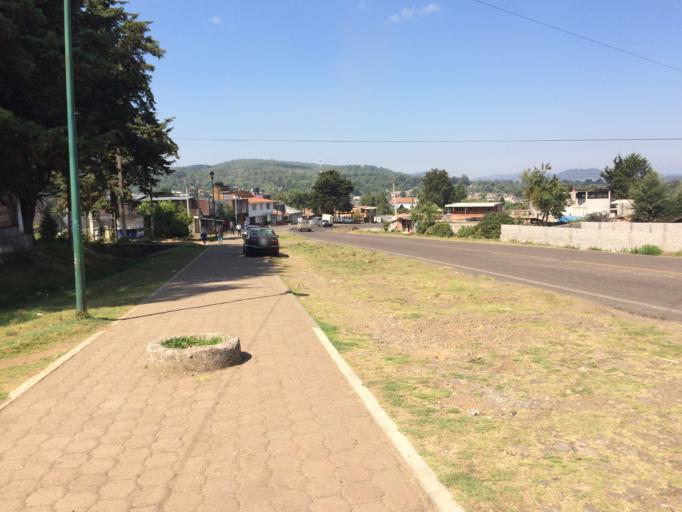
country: MX
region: Michoacan
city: Opopeo
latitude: 19.4156
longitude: -101.6028
